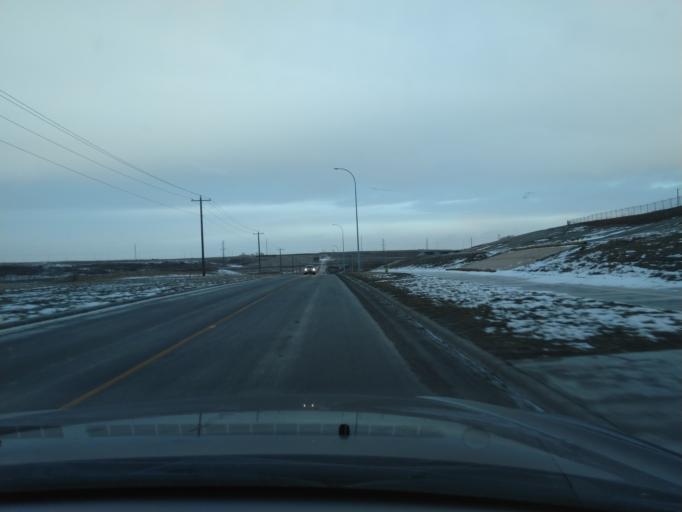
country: CA
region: Alberta
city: Calgary
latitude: 51.1658
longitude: -114.0247
